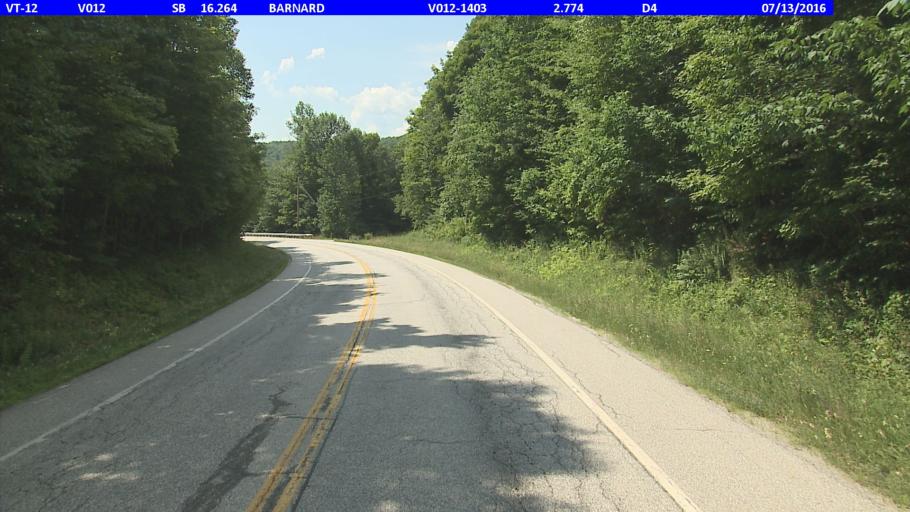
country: US
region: Vermont
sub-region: Windsor County
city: Woodstock
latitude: 43.7019
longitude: -72.6196
